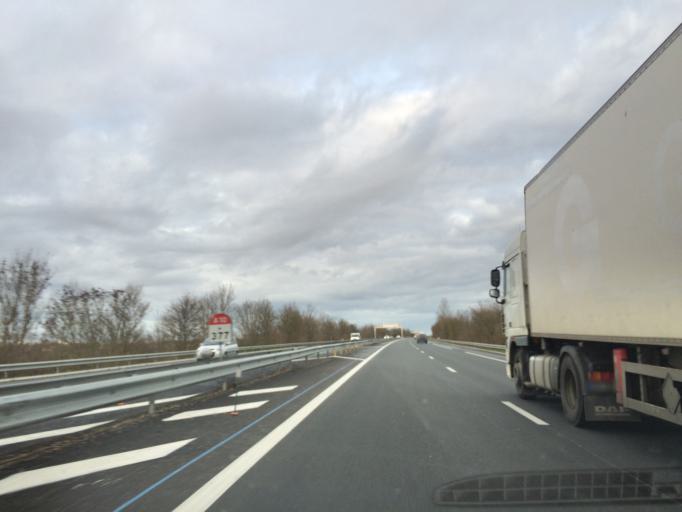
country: FR
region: Poitou-Charentes
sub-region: Departement des Deux-Sevres
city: Fors
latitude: 46.2599
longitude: -0.4183
